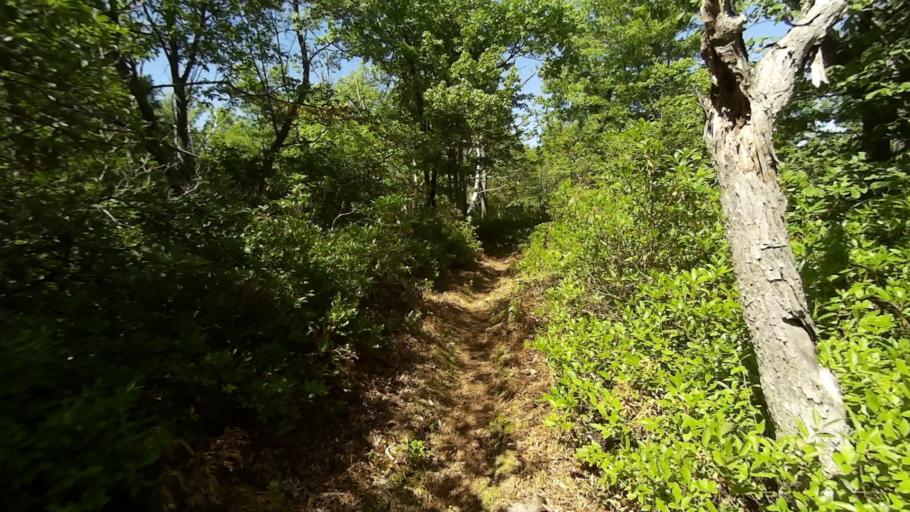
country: US
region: Pennsylvania
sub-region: Centre County
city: Boalsburg
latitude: 40.7194
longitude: -77.7825
